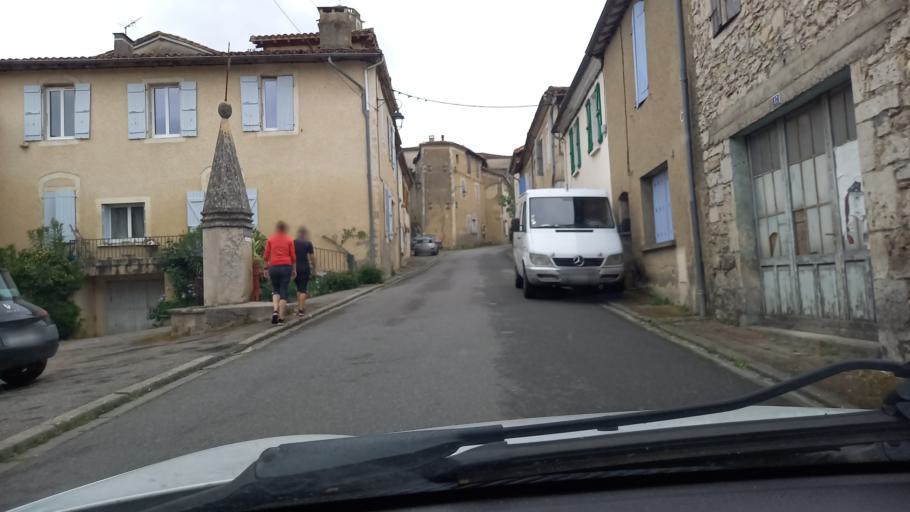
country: FR
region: Midi-Pyrenees
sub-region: Departement du Gers
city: Gimont
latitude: 43.7306
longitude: 0.8747
